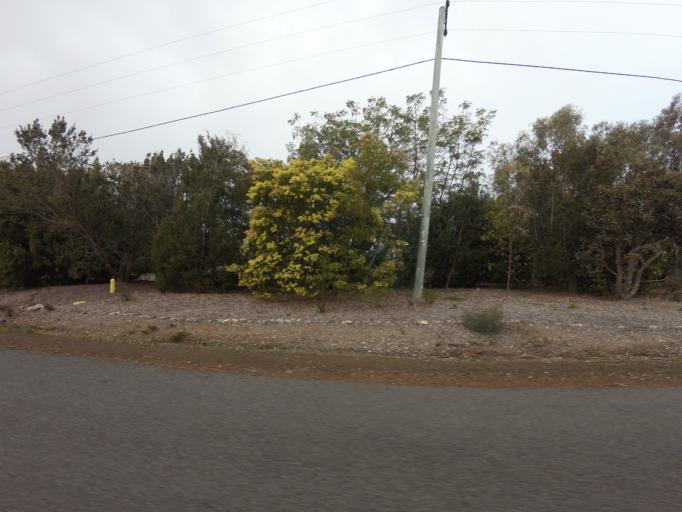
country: AU
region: Tasmania
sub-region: Sorell
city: Sorell
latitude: -42.5330
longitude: 147.9123
